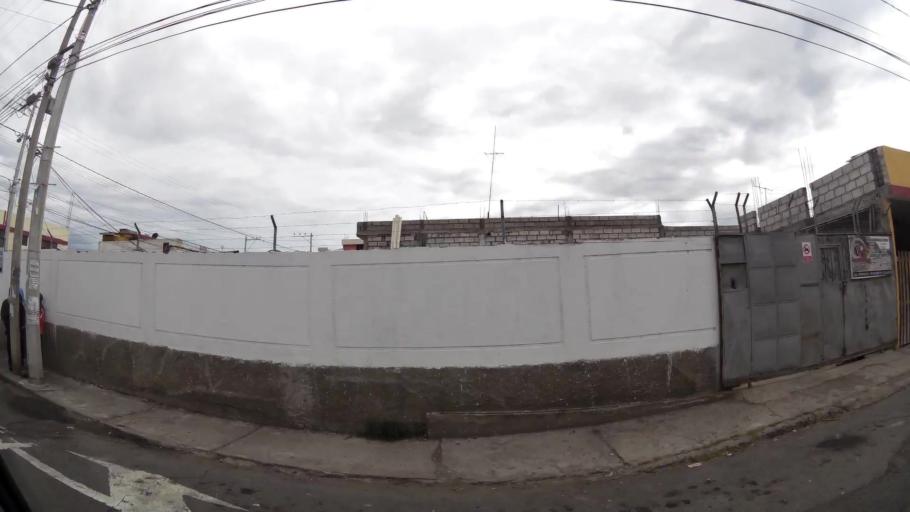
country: EC
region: Cotopaxi
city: Latacunga
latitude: -0.9296
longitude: -78.6260
